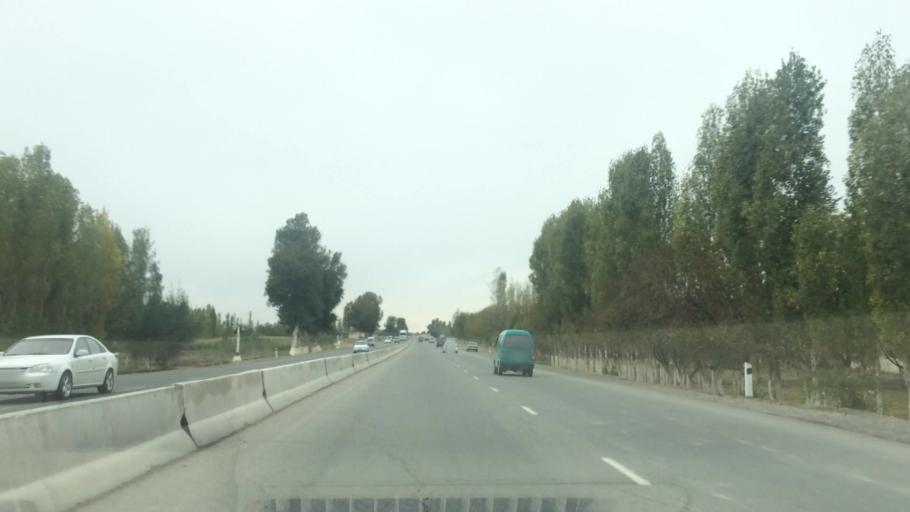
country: UZ
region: Samarqand
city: Jomboy
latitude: 39.7306
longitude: 67.1546
